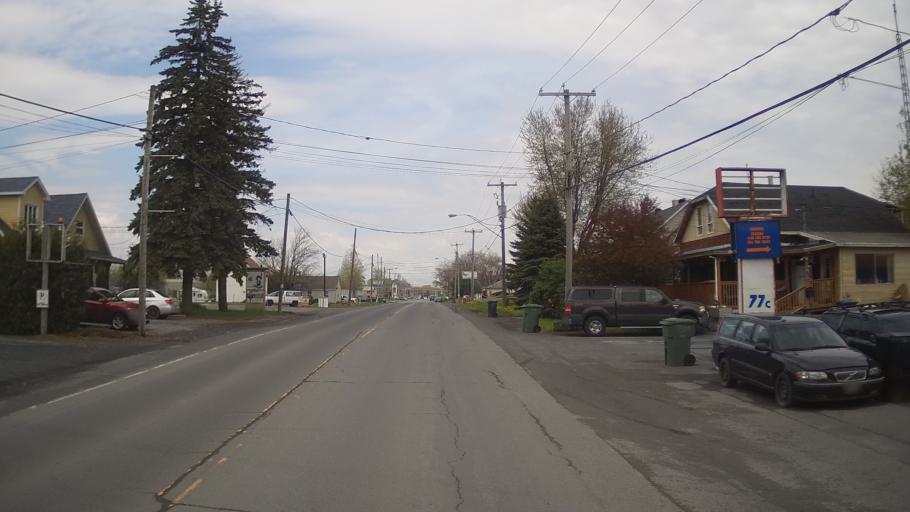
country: CA
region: Quebec
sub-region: Monteregie
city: Saint-Jean-sur-Richelieu
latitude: 45.3128
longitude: -73.2147
